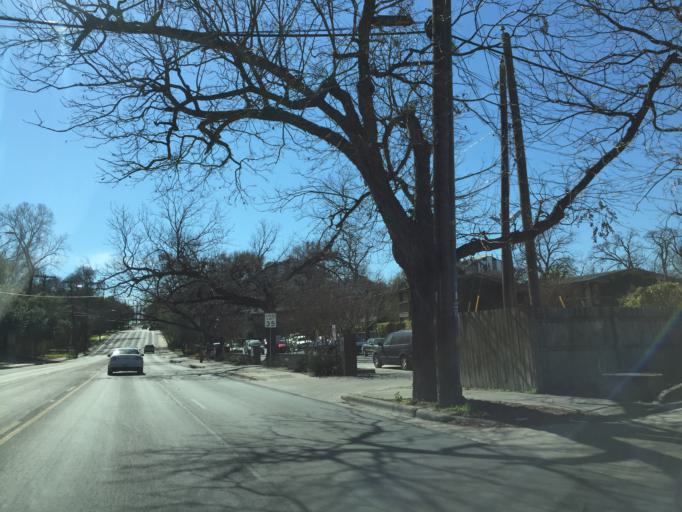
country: US
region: Texas
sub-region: Travis County
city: Austin
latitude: 30.2580
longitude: -97.7504
